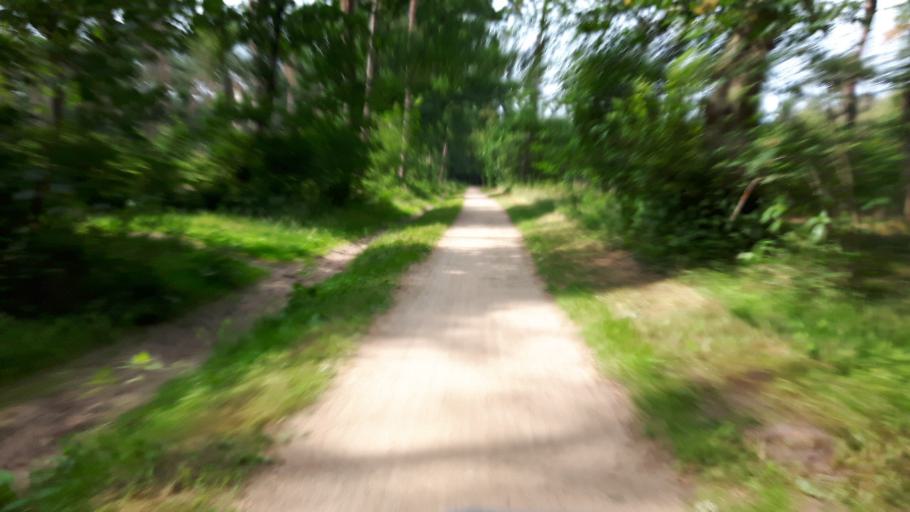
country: NL
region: North Holland
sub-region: Gemeente Hilversum
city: Hilversum
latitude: 52.1810
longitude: 5.1932
